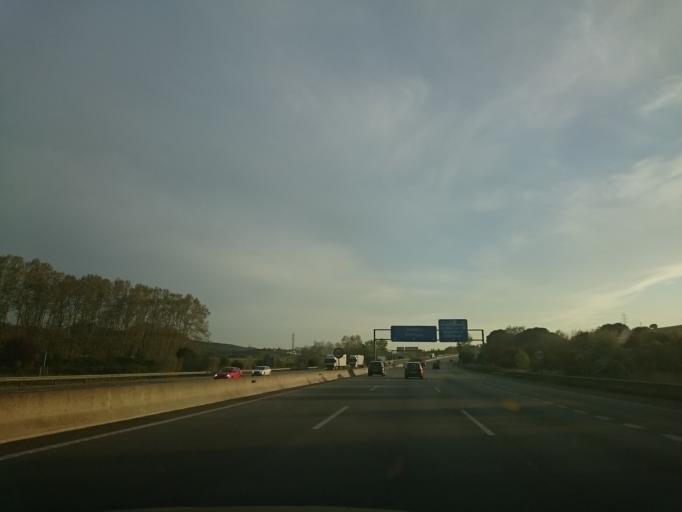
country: ES
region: Catalonia
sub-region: Provincia de Barcelona
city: La Roca del Valles
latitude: 41.6077
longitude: 2.3437
